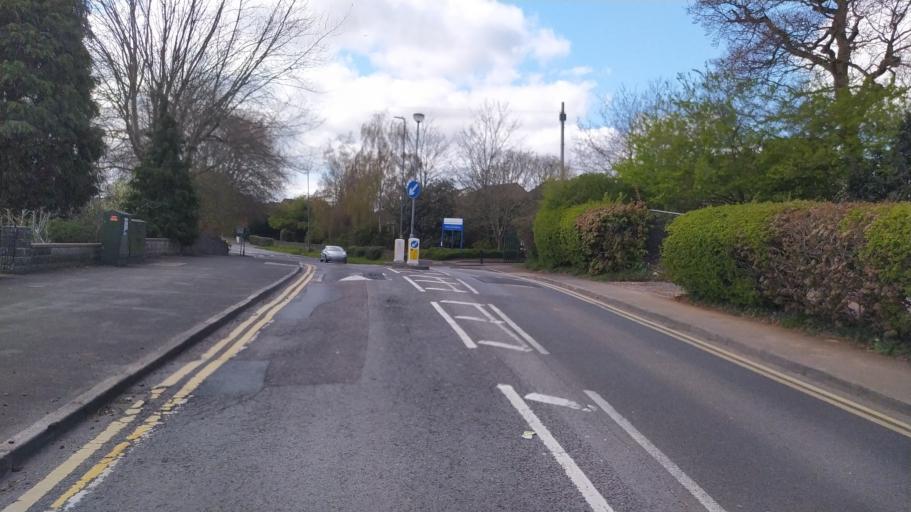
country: GB
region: England
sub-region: South Gloucestershire
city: Kingswood
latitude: 51.4474
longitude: -2.4875
